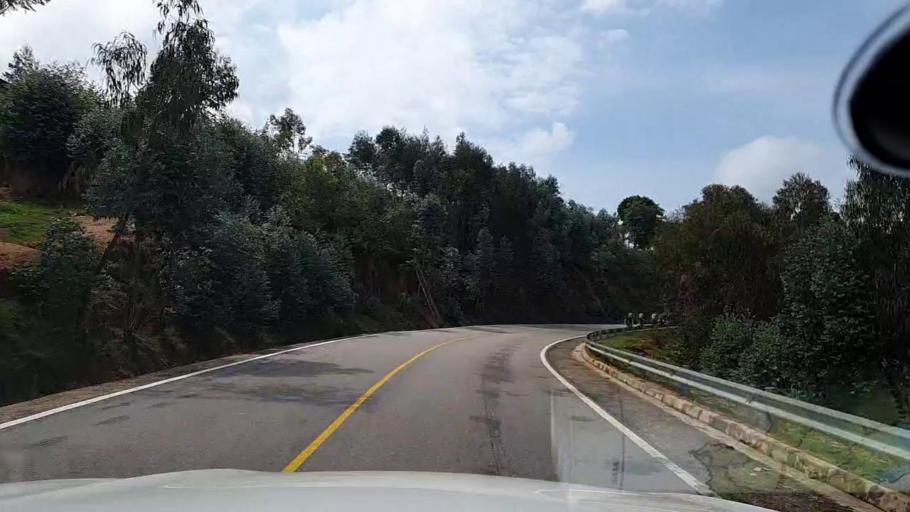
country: RW
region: Southern Province
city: Nzega
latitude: -2.5055
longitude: 29.5012
